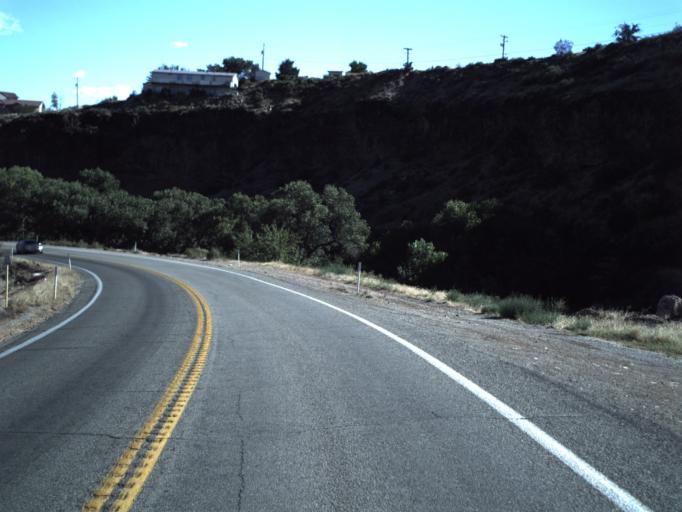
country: US
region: Utah
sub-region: Washington County
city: LaVerkin
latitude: 37.2258
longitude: -113.2818
